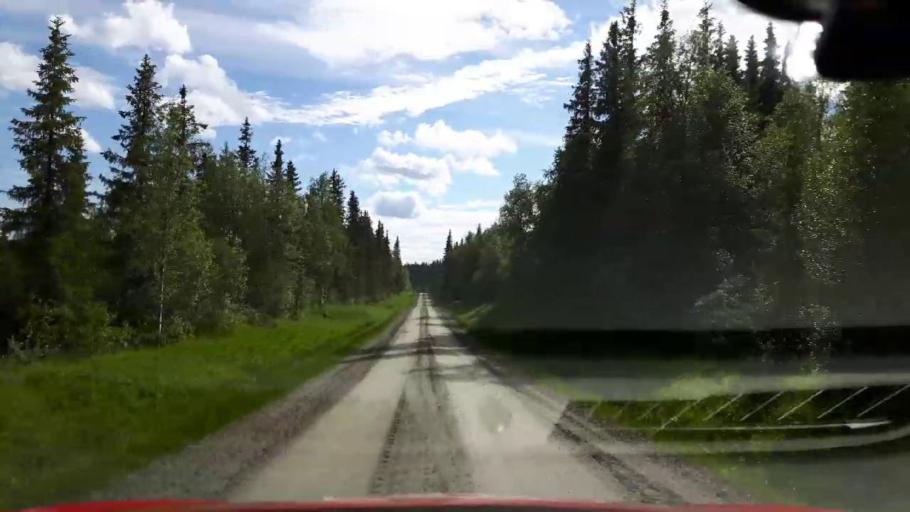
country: SE
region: Jaemtland
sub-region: Krokoms Kommun
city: Valla
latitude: 63.8536
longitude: 14.0885
